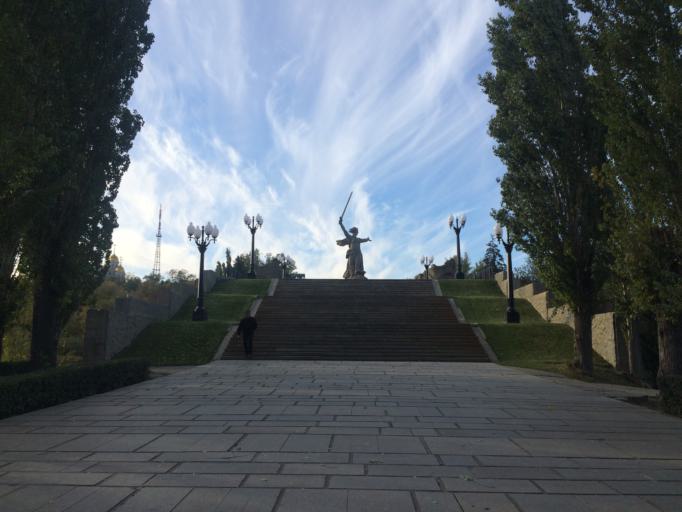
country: RU
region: Volgograd
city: Volgograd
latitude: 48.7403
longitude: 44.5432
